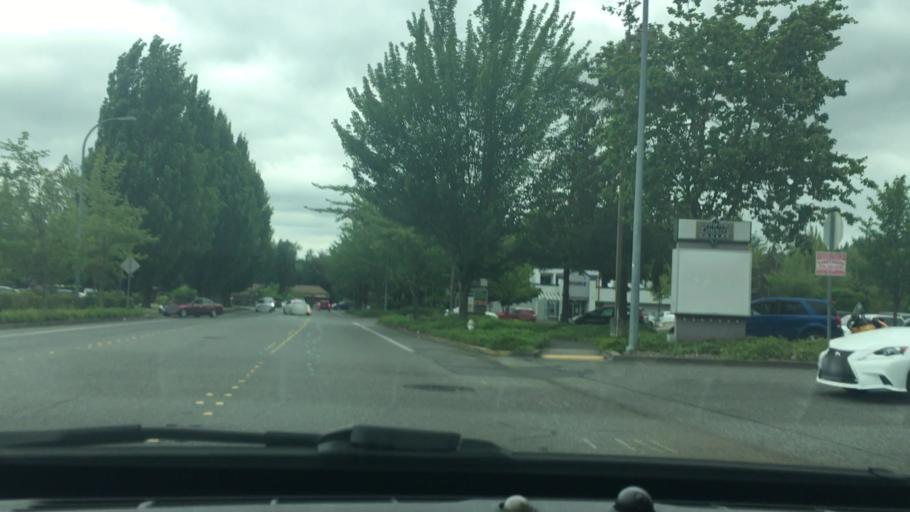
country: US
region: Washington
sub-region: King County
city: Issaquah
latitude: 47.5443
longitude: -122.0574
